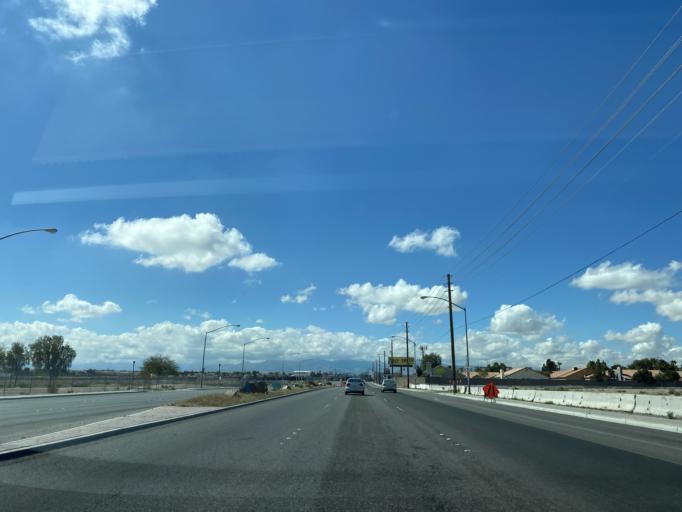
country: US
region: Nevada
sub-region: Clark County
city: North Las Vegas
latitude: 36.2397
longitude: -115.1281
